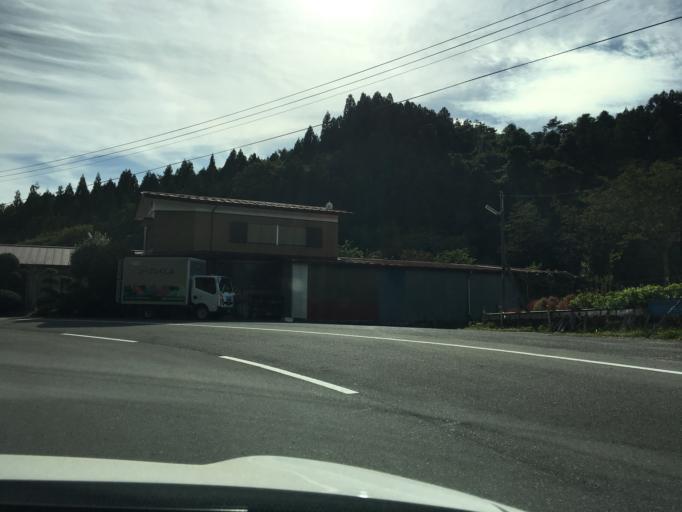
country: JP
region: Fukushima
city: Nihommatsu
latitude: 37.5335
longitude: 140.5061
